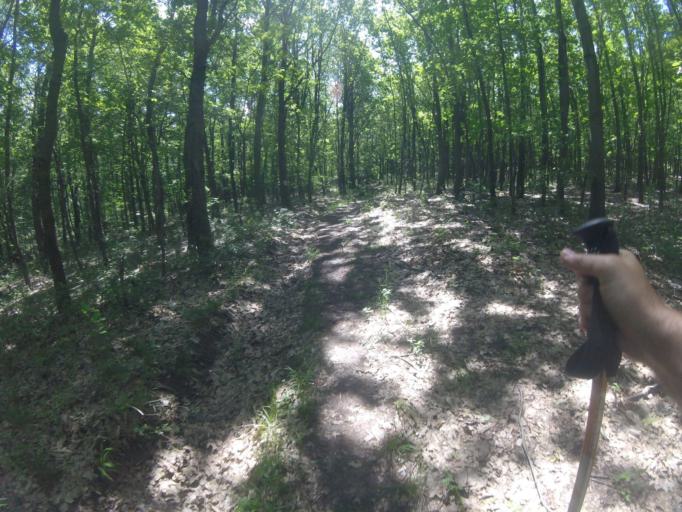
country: HU
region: Nograd
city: Matraverebely
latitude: 47.9329
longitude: 19.7955
